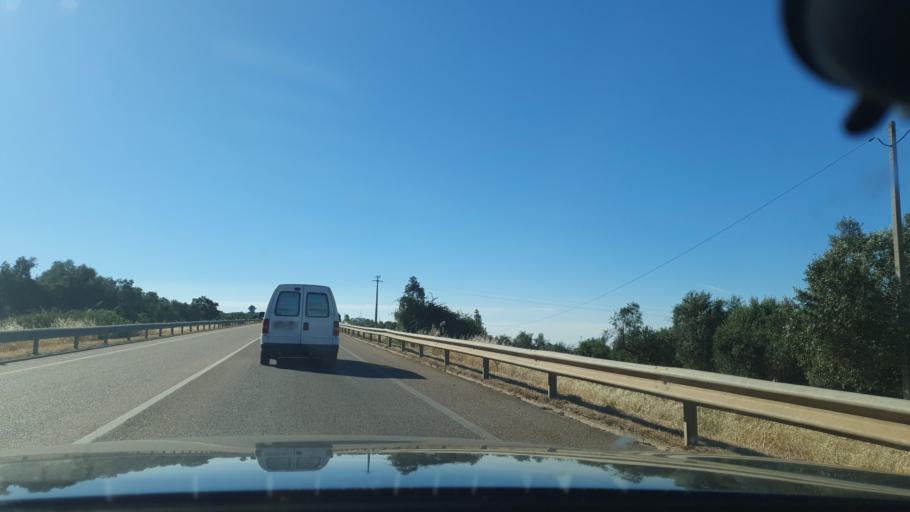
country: PT
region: Evora
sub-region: Vila Vicosa
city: Vila Vicosa
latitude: 38.7713
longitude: -7.4317
